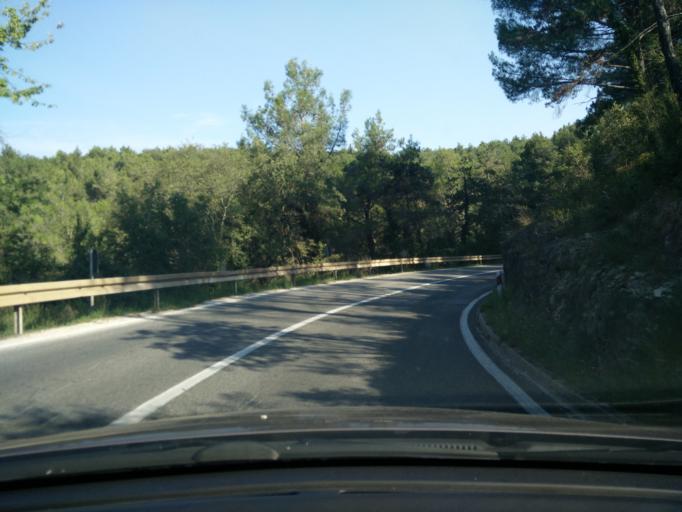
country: HR
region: Istarska
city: Novigrad
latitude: 45.3150
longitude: 13.6184
